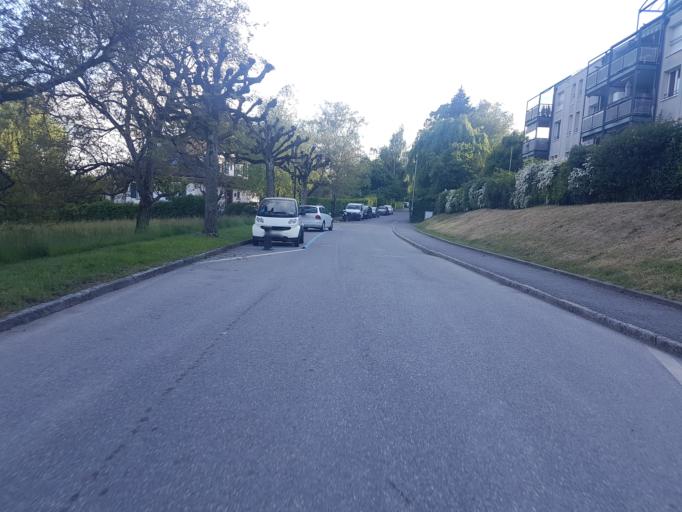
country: CH
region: Geneva
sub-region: Geneva
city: Vernier
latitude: 46.2163
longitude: 6.0923
